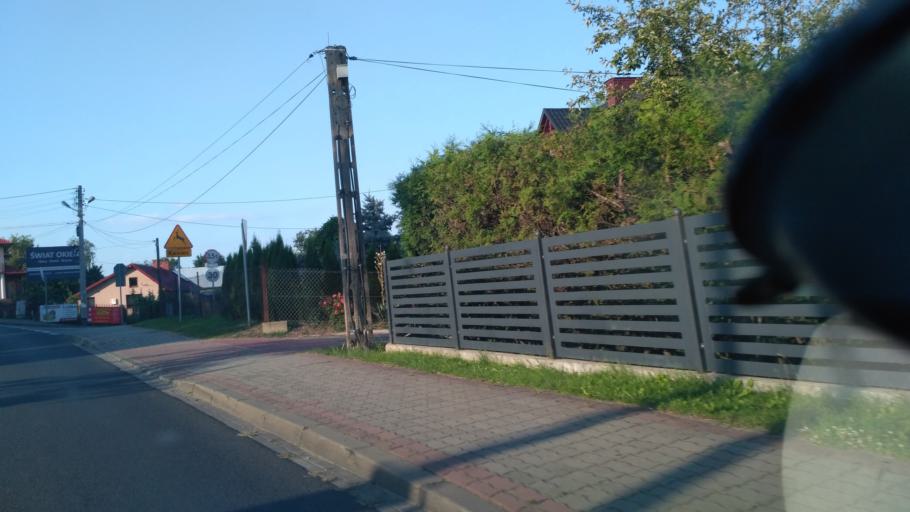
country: PL
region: Subcarpathian Voivodeship
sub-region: Powiat lezajski
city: Stare Miasto
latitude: 50.2820
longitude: 22.4303
